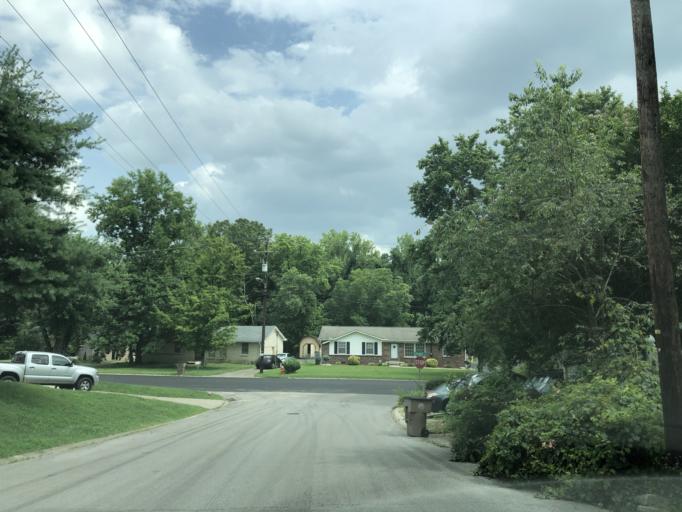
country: US
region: Tennessee
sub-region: Williamson County
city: Brentwood Estates
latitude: 36.0550
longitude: -86.6810
